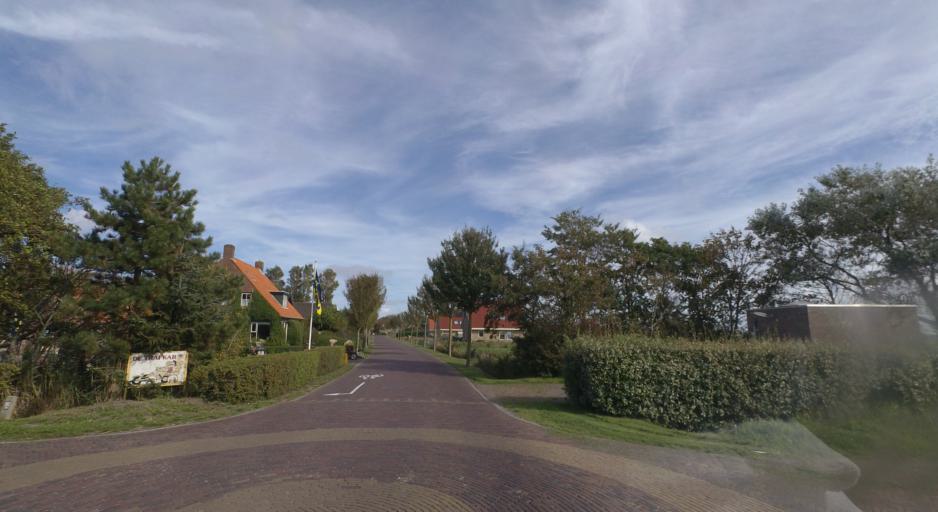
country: NL
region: Friesland
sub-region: Gemeente Ameland
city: Nes
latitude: 53.4470
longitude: 5.7928
